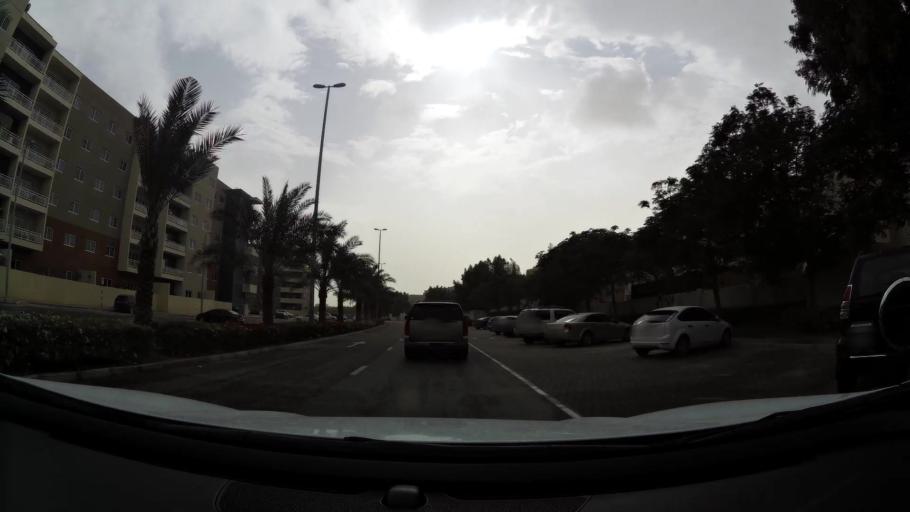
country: AE
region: Abu Dhabi
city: Abu Dhabi
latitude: 24.4550
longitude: 54.6712
